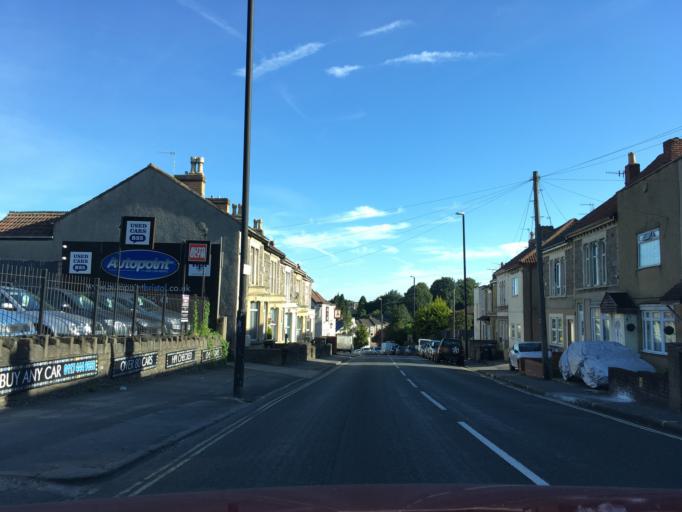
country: GB
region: England
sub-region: South Gloucestershire
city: Kingswood
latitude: 51.4553
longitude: -2.5285
